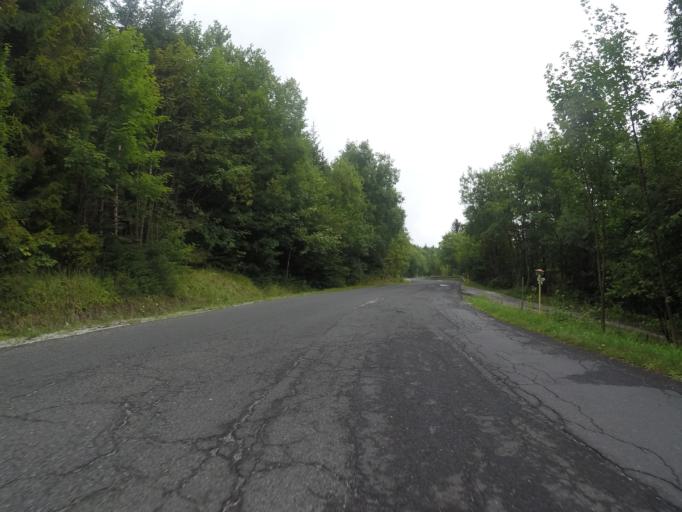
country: SK
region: Kosicky
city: Spisska Nova Ves
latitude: 48.8603
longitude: 20.5230
